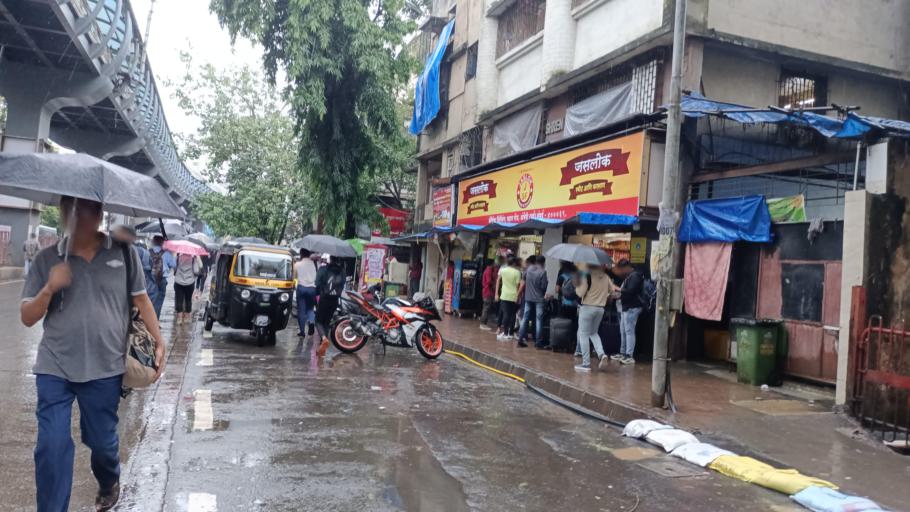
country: IN
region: Maharashtra
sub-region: Mumbai Suburban
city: Mumbai
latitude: 19.1177
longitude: 72.8479
